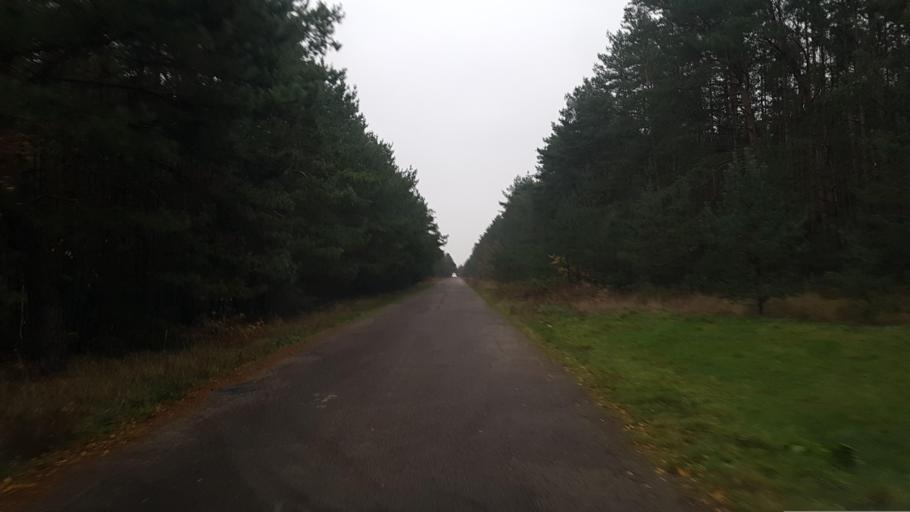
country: DE
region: Brandenburg
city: Ruhland
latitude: 51.4303
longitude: 13.8706
